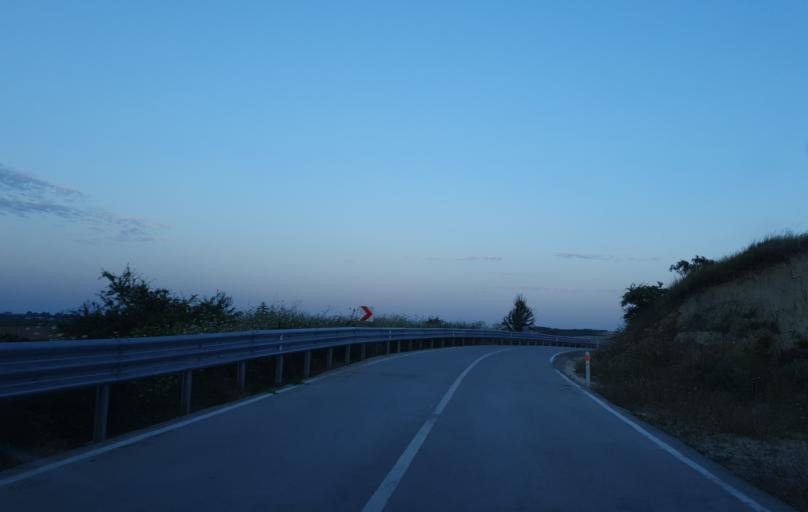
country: TR
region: Tekirdag
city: Velimese
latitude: 41.3545
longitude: 27.8547
